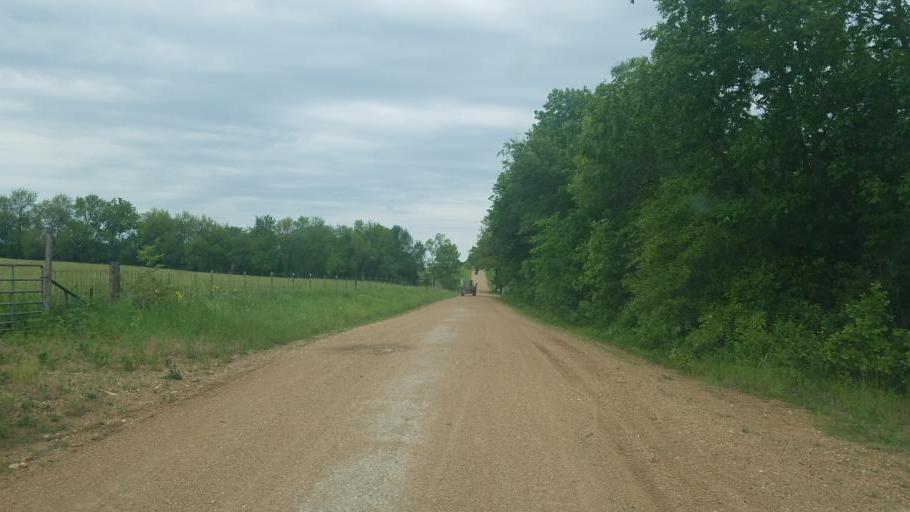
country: US
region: Missouri
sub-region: Moniteau County
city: Tipton
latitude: 38.5585
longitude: -92.7284
